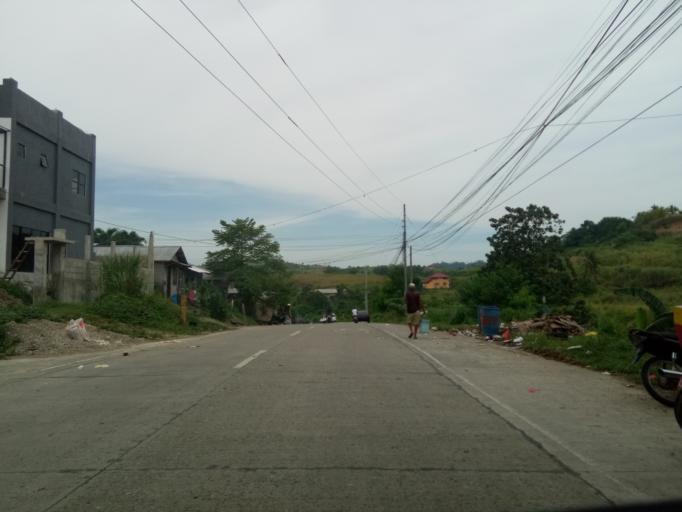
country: PH
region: Caraga
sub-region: Province of Surigao del Norte
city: Surigao
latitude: 9.7733
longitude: 125.4913
